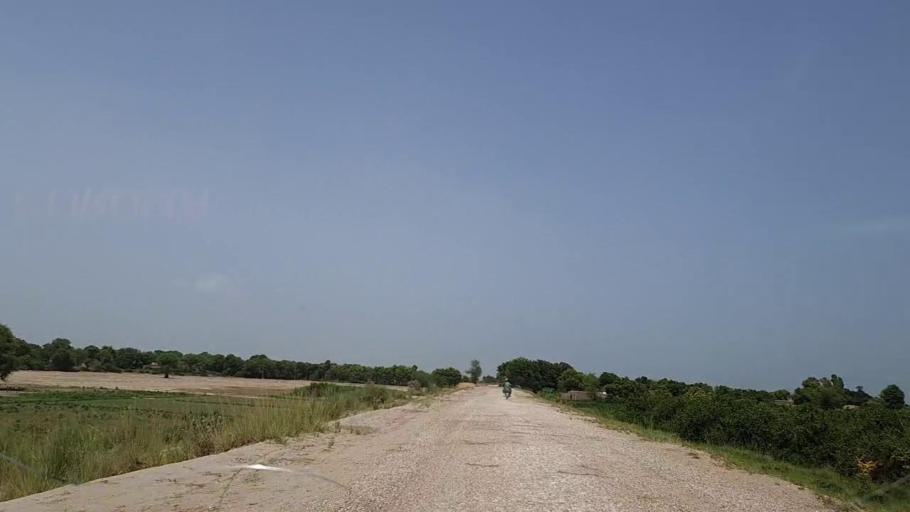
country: PK
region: Sindh
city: Kandiaro
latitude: 27.0425
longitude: 68.1130
